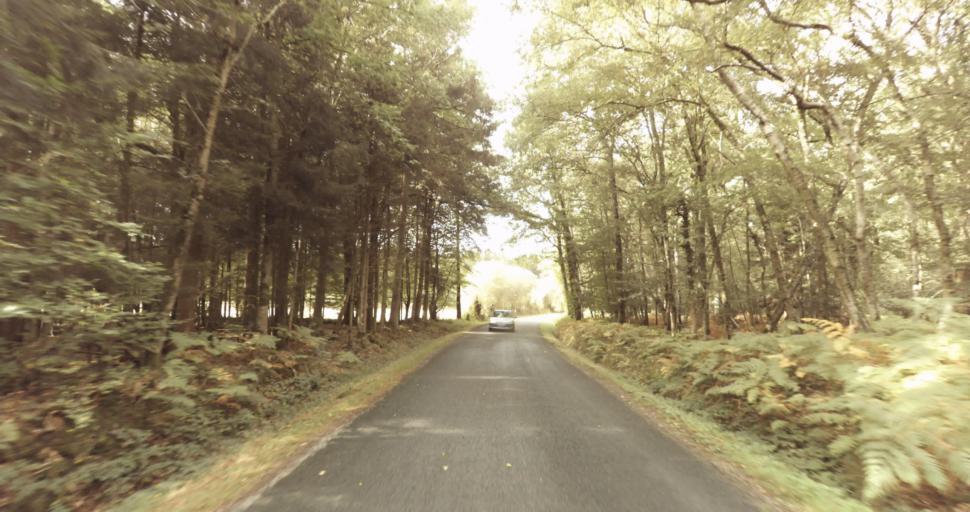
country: FR
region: Lower Normandy
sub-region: Departement de l'Orne
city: Sainte-Gauburge-Sainte-Colombe
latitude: 48.7825
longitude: 0.3851
